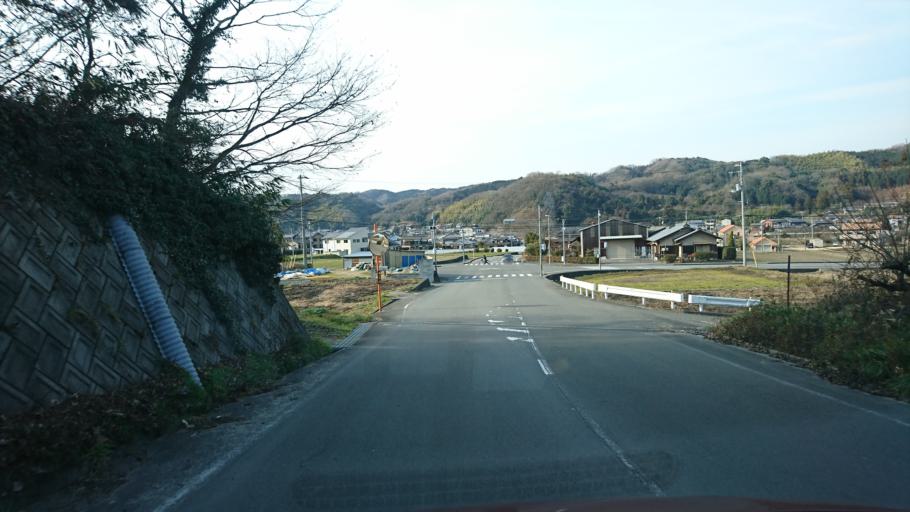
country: JP
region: Ehime
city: Hojo
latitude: 34.0241
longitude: 132.9619
